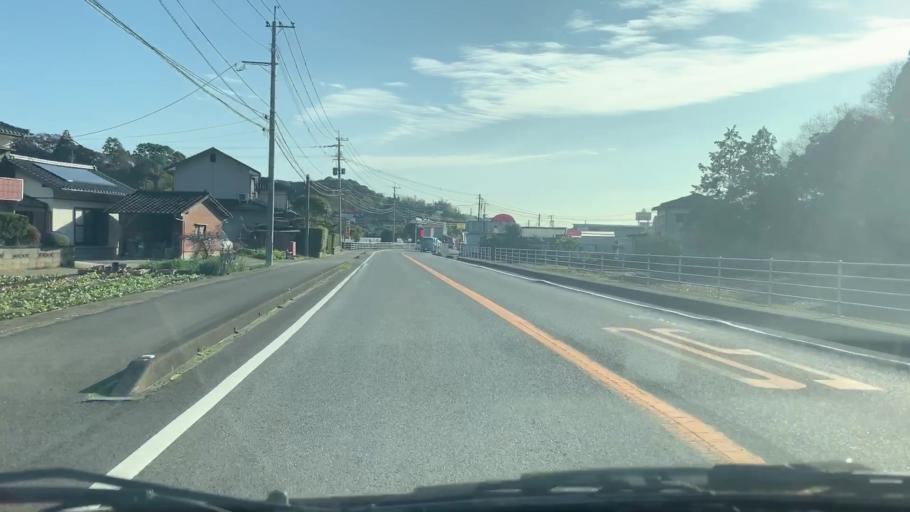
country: JP
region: Saga Prefecture
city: Takeocho-takeo
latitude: 33.2257
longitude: 130.0415
